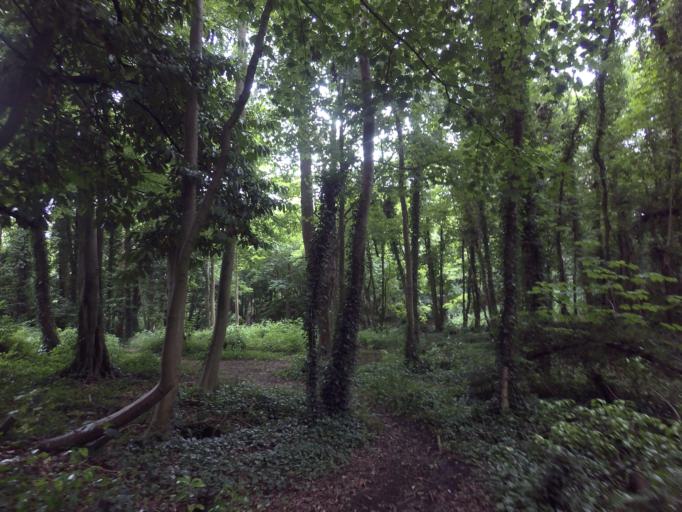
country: IE
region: Leinster
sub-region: Fingal County
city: Blanchardstown
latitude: 53.3880
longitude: -6.3719
